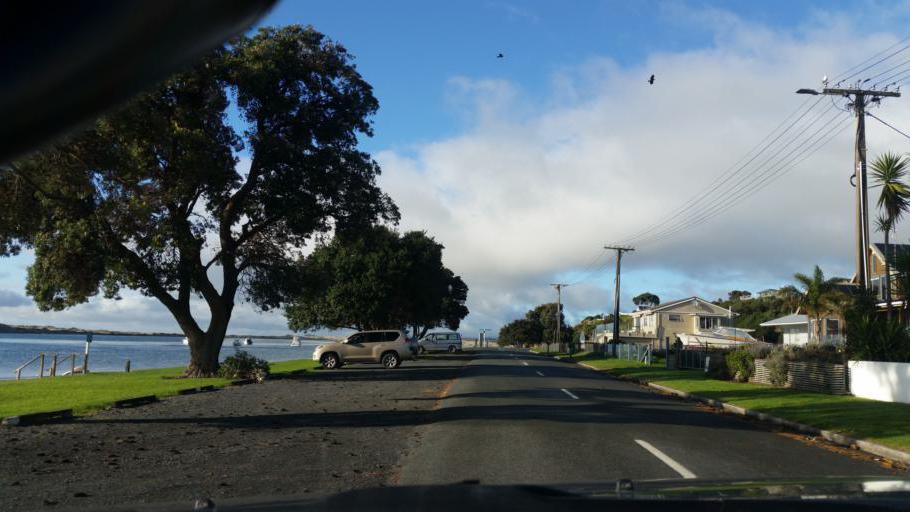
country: NZ
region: Auckland
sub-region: Auckland
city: Wellsford
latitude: -36.0893
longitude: 174.5895
